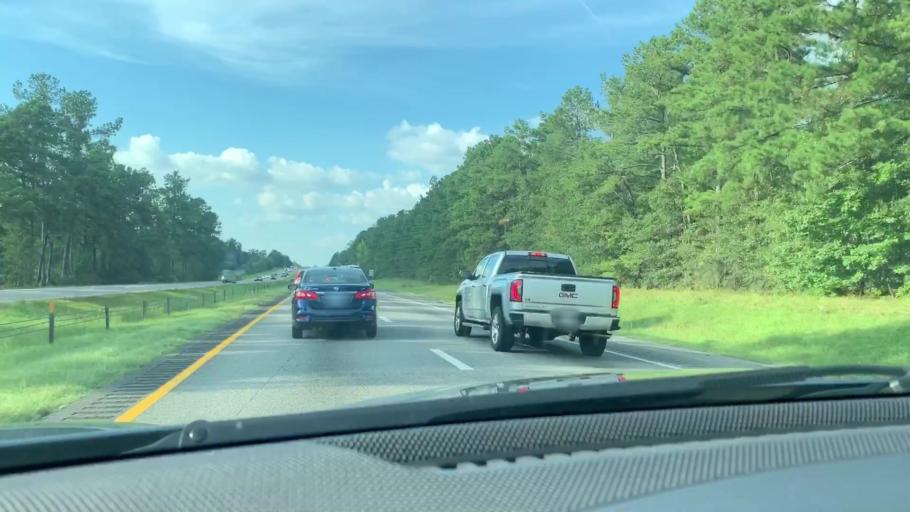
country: US
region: South Carolina
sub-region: Calhoun County
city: Saint Matthews
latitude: 33.6125
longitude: -80.8652
